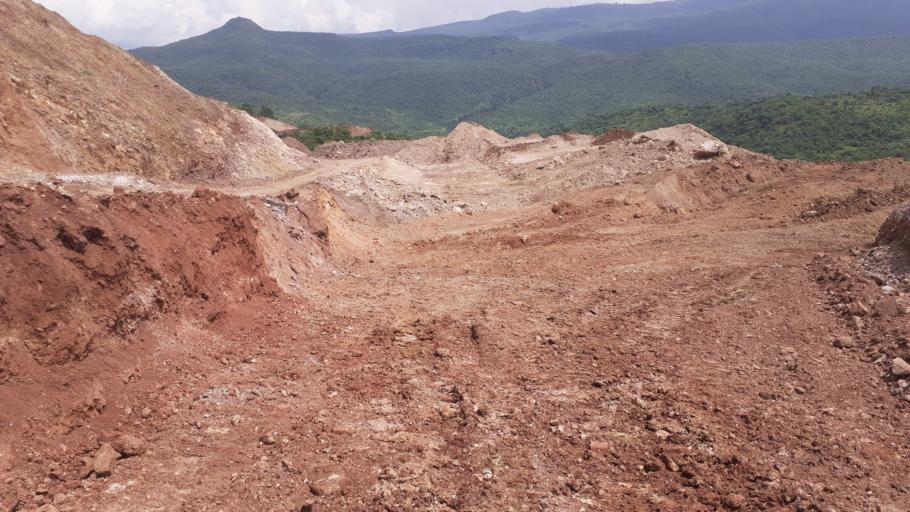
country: ET
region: Southern Nations, Nationalities, and People's Region
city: Areka
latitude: 7.6164
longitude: 37.5237
